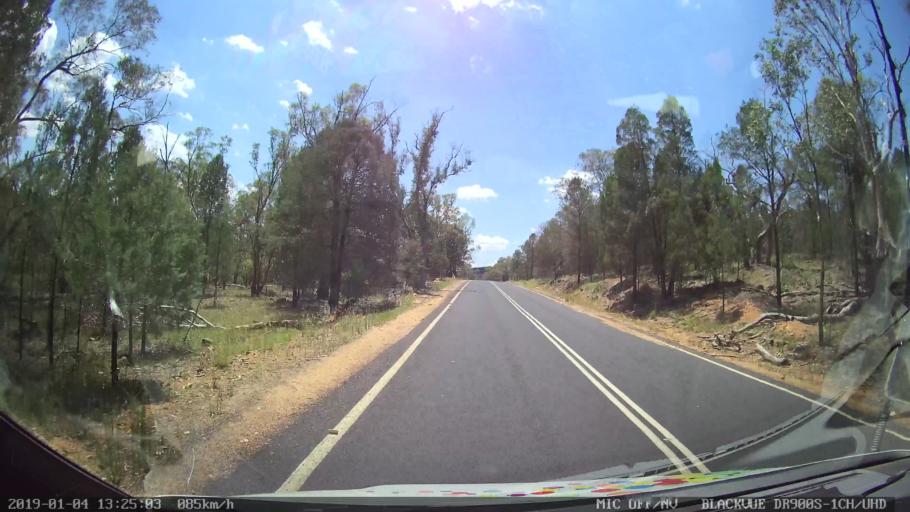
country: AU
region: New South Wales
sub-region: Parkes
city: Peak Hill
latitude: -32.6978
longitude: 148.5544
